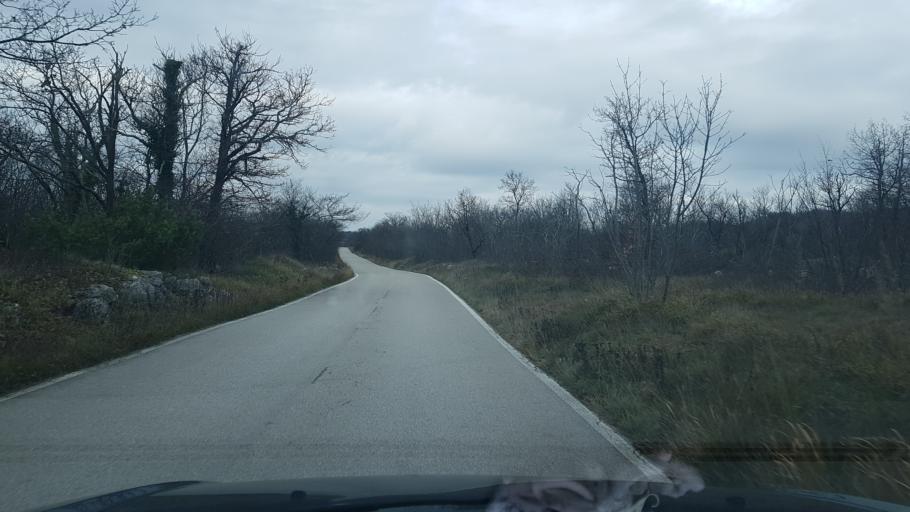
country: IT
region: Friuli Venezia Giulia
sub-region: Provincia di Trieste
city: Zolla
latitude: 45.7046
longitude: 13.8240
